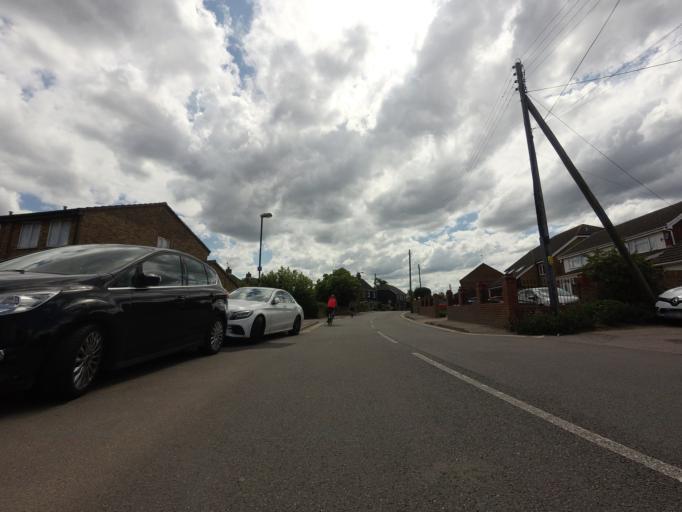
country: GB
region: England
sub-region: Kent
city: Hoo
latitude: 51.4213
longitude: 0.5655
